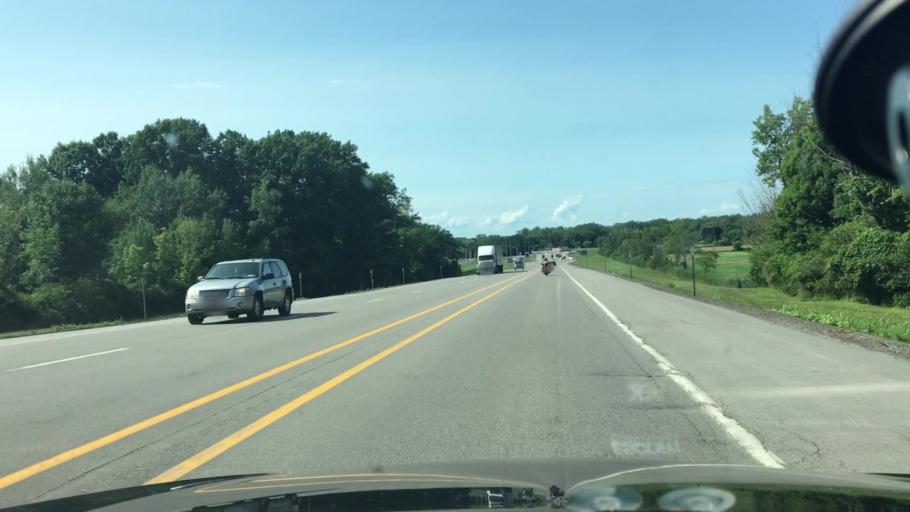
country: US
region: New York
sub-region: Chautauqua County
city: Silver Creek
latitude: 42.5555
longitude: -79.1129
